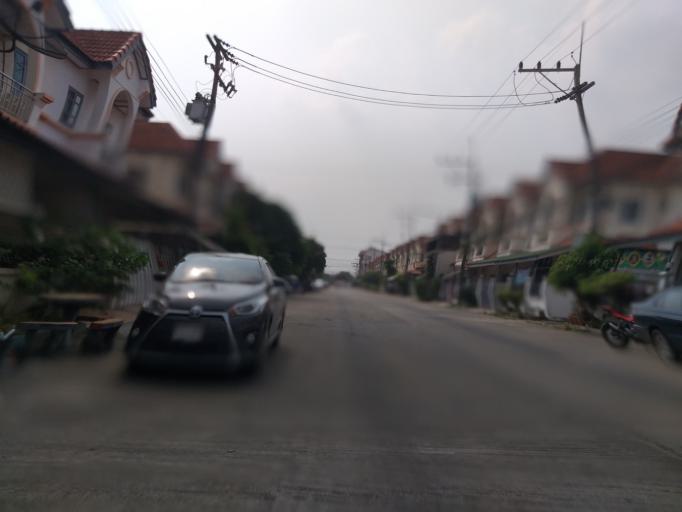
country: TH
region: Pathum Thani
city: Nong Suea
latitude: 14.0670
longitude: 100.8587
